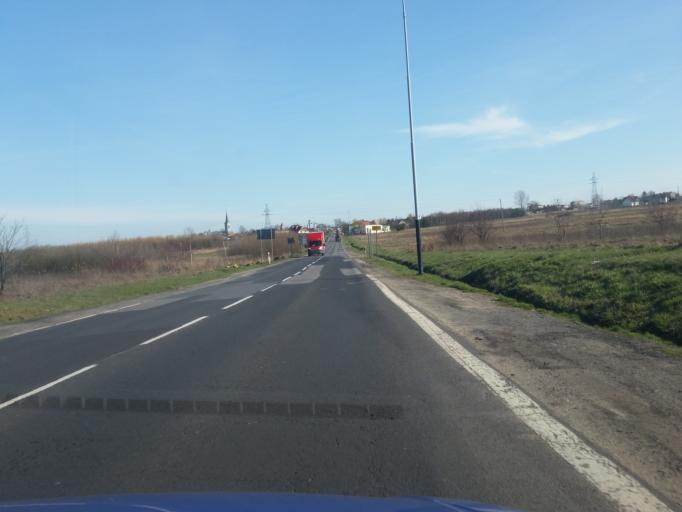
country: PL
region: Lodz Voivodeship
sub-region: Powiat radomszczanski
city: Kamiensk
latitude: 51.2109
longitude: 19.4875
